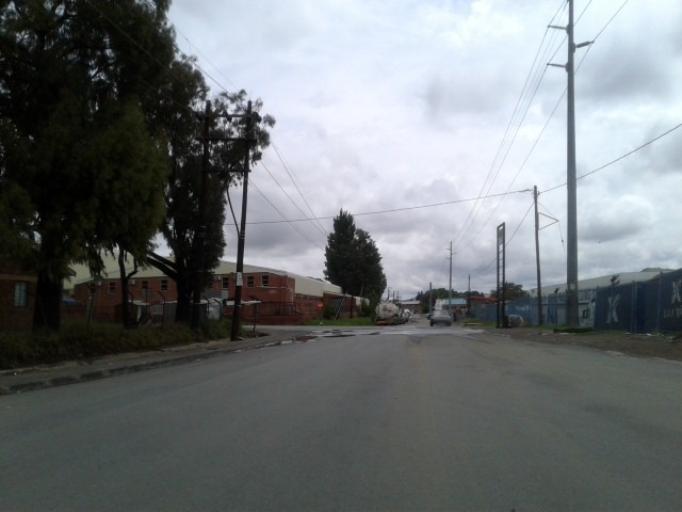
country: LS
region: Maseru
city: Maseru
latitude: -29.2974
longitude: 27.4771
